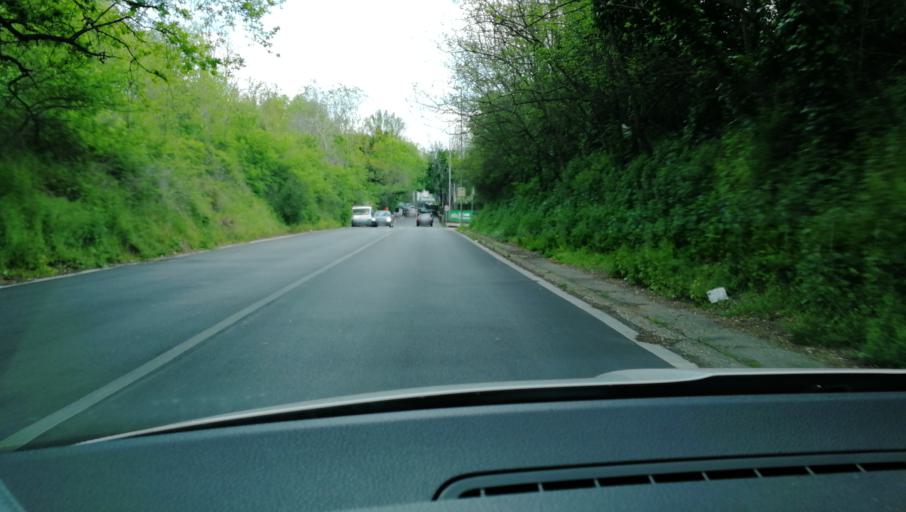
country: IT
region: Latium
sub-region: Citta metropolitana di Roma Capitale
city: Rome
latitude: 41.8543
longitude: 12.5296
